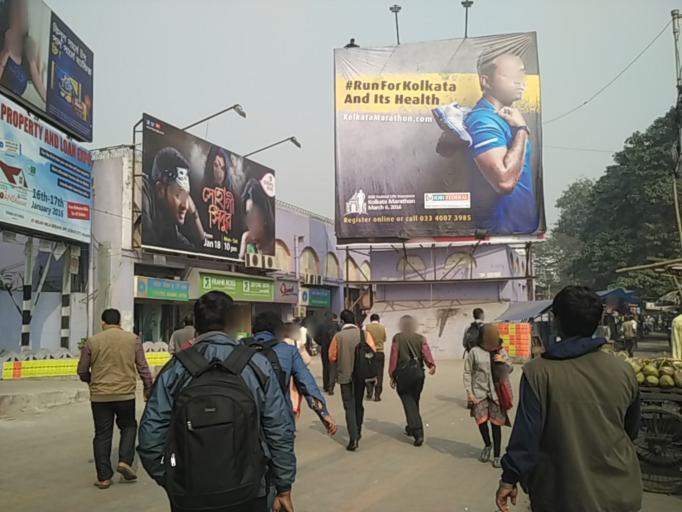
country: IN
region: West Bengal
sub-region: Kolkata
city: Kolkata
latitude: 22.4938
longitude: 88.3452
